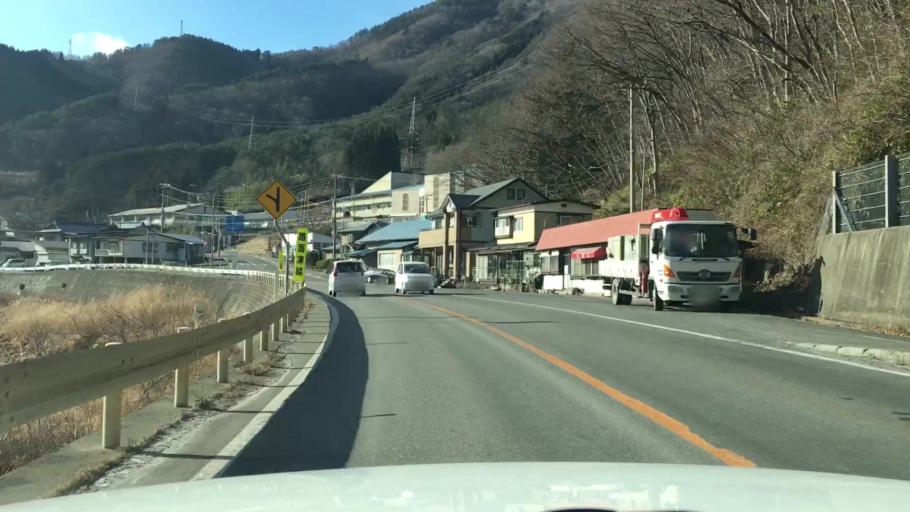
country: JP
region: Iwate
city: Miyako
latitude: 39.5999
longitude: 141.6826
